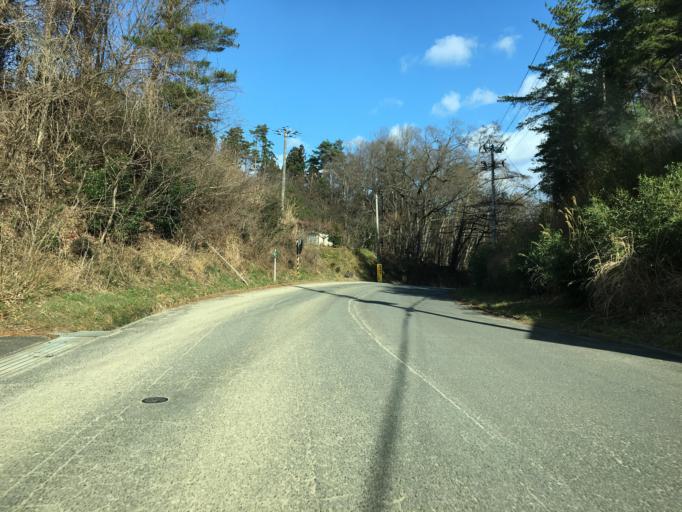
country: JP
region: Fukushima
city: Nihommatsu
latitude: 37.5854
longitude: 140.4023
